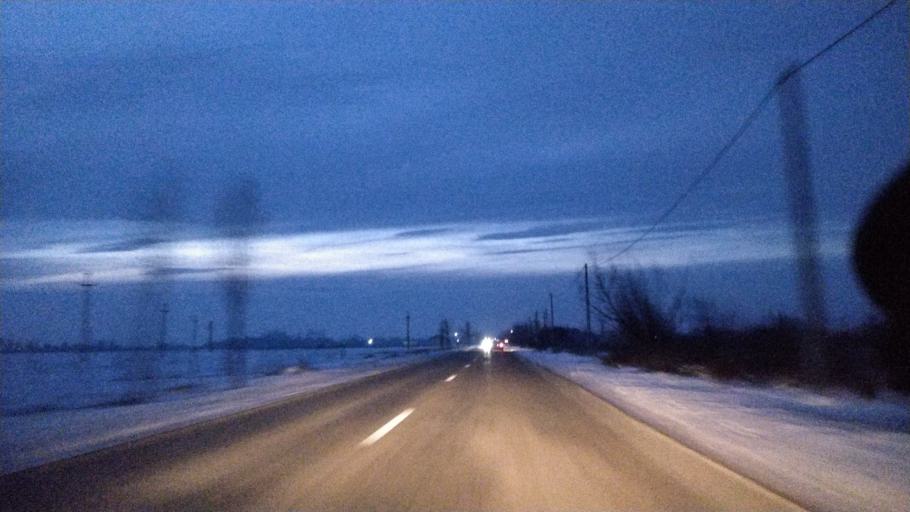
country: RO
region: Vrancea
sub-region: Comuna Rastoaca
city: Rastoaca
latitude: 45.6537
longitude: 27.3030
